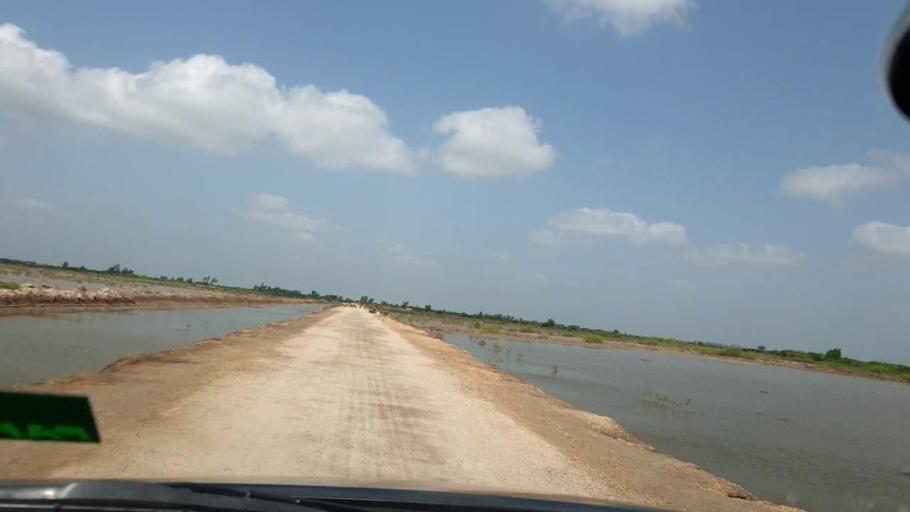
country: PK
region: Sindh
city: Kadhan
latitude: 24.5970
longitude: 69.1285
